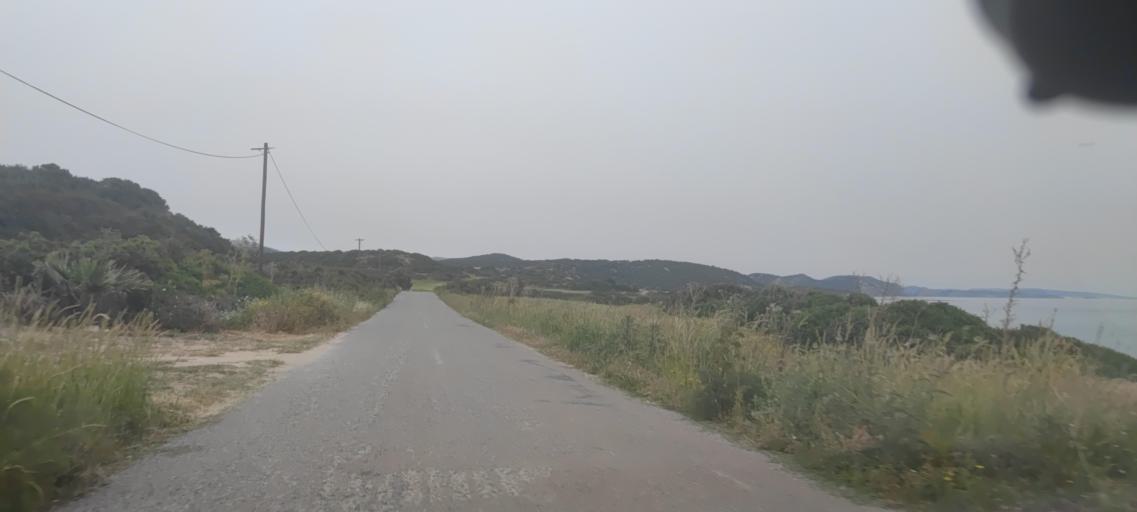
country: CY
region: Ammochostos
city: Rizokarpaso
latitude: 35.5906
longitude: 34.4230
